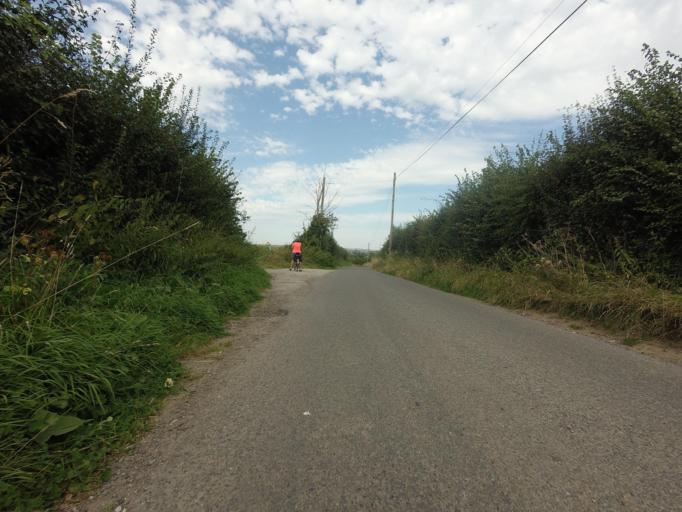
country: GB
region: England
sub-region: Wiltshire
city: Holt
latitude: 51.3421
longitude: -2.1751
